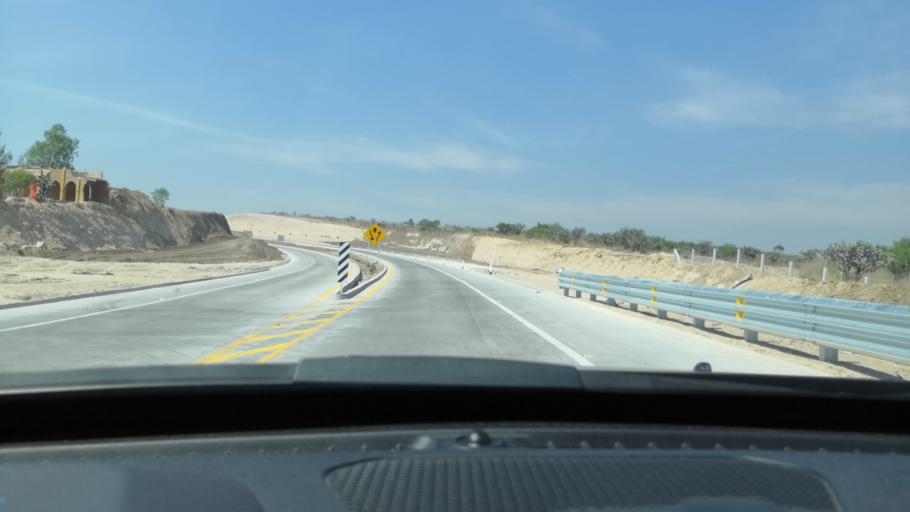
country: MX
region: Guanajuato
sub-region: Purisima del Rincon
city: Potrerillos (Guanajal)
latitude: 21.0862
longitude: -101.8534
